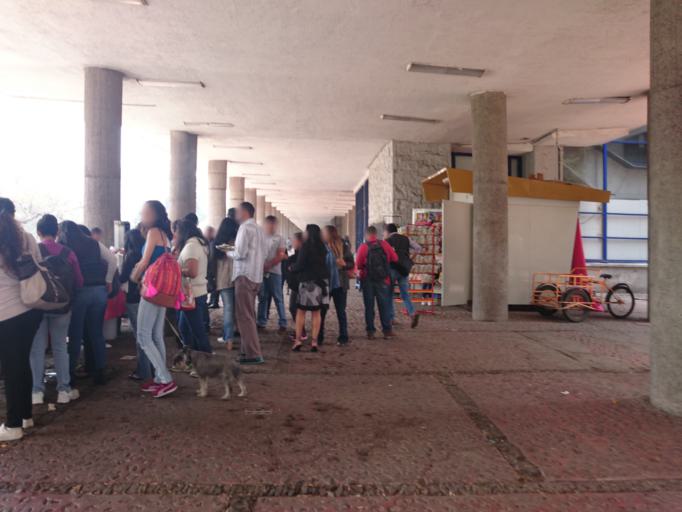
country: MX
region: Mexico City
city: Coyoacan
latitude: 19.3343
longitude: -99.1840
